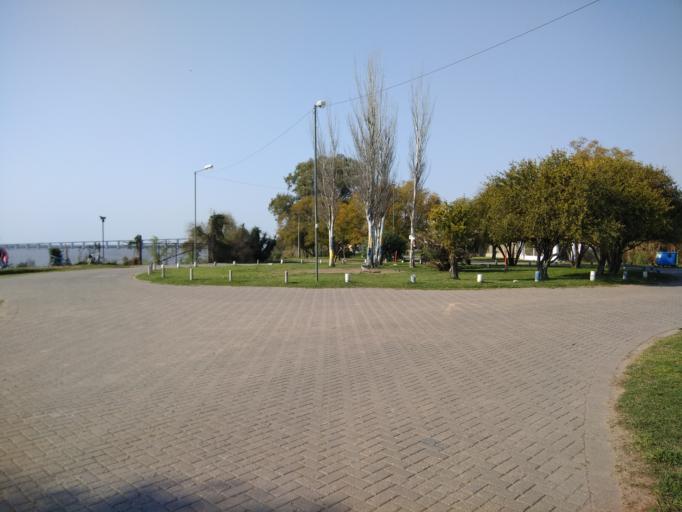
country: AR
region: Santa Fe
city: Granadero Baigorria
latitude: -32.8489
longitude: -60.6967
